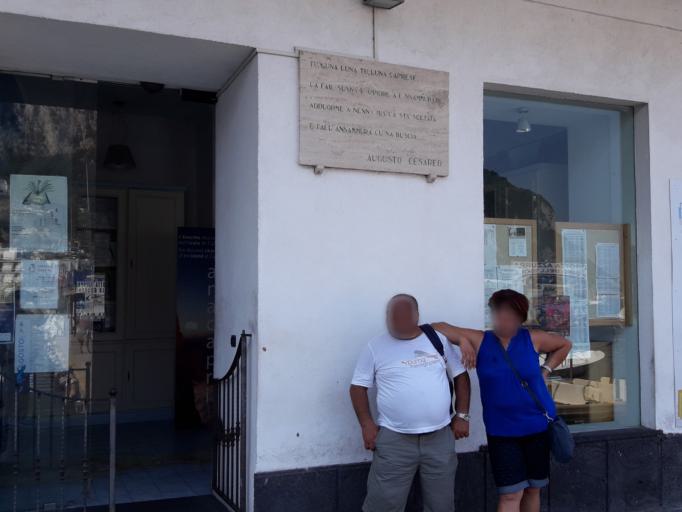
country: IT
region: Campania
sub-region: Provincia di Napoli
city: Capri
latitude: 40.5565
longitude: 14.2390
